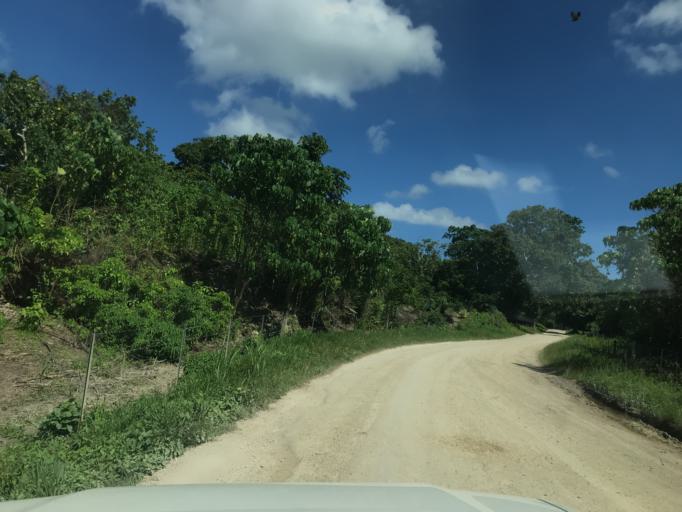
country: VU
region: Sanma
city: Luganville
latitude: -15.5791
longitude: 167.0351
